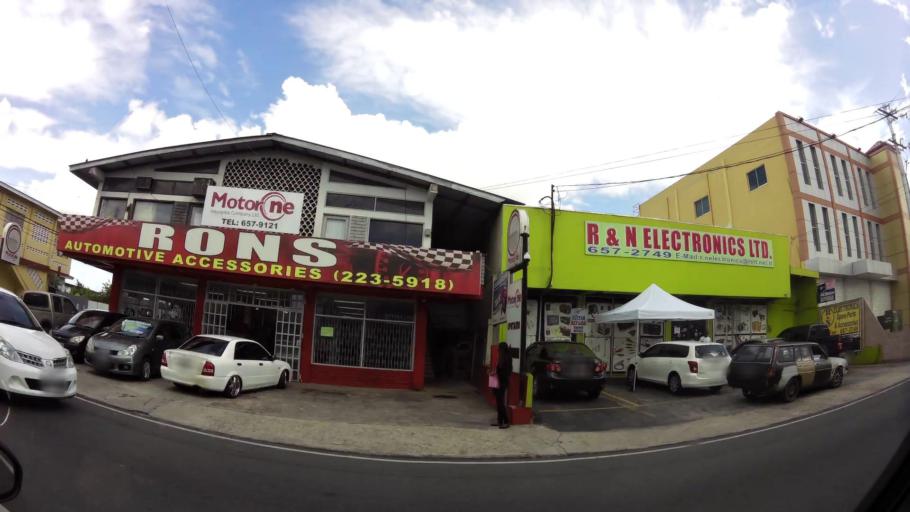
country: TT
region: City of San Fernando
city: San Fernando
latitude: 10.2737
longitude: -61.4609
